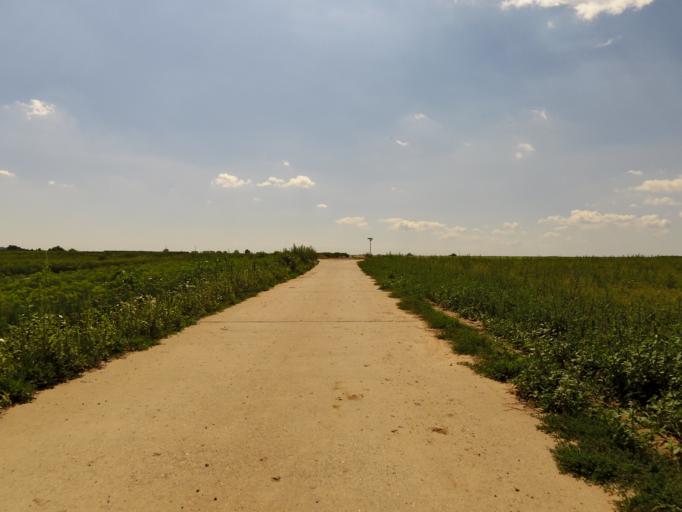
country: DE
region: Rheinland-Pfalz
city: Ellerstadt
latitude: 49.4505
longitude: 8.2625
